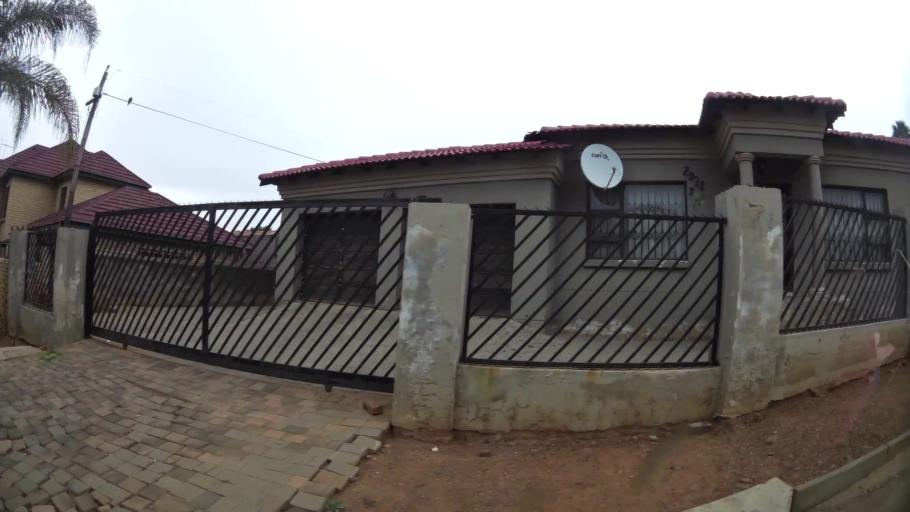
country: ZA
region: Gauteng
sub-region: City of Tshwane Metropolitan Municipality
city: Pretoria
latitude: -25.7033
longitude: 28.3526
